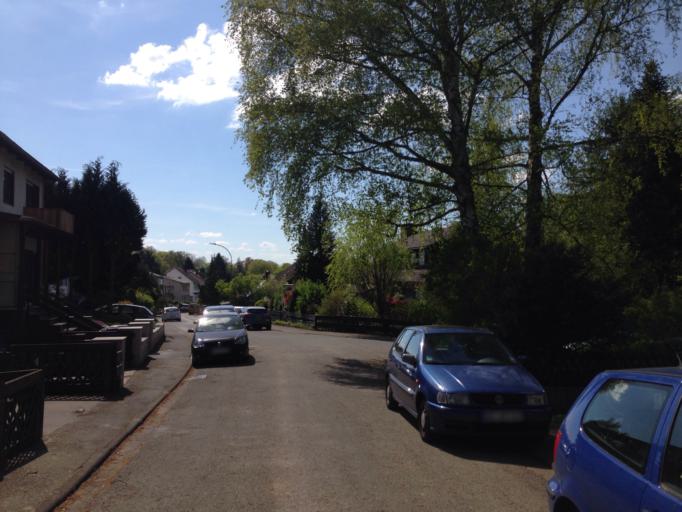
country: DE
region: Hesse
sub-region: Regierungsbezirk Giessen
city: Laubach
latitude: 50.5460
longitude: 8.9993
